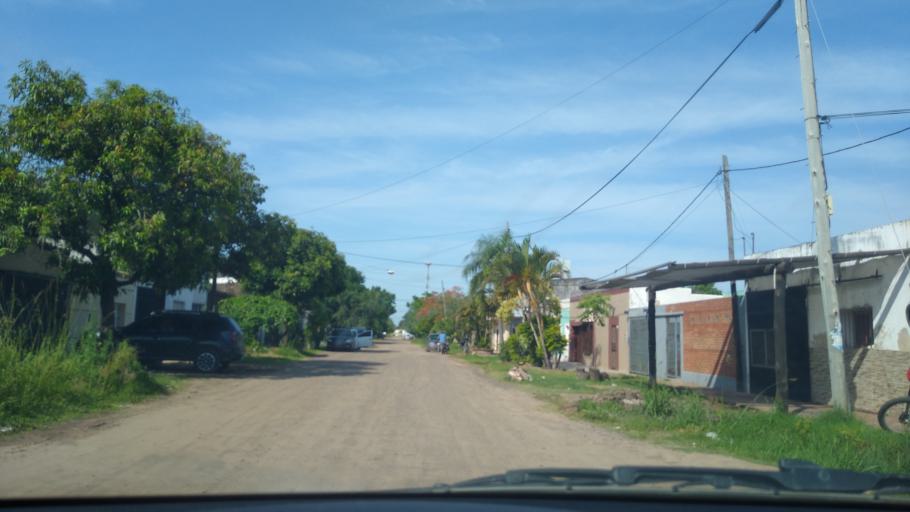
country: AR
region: Chaco
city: Barranqueras
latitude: -27.4870
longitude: -58.9459
